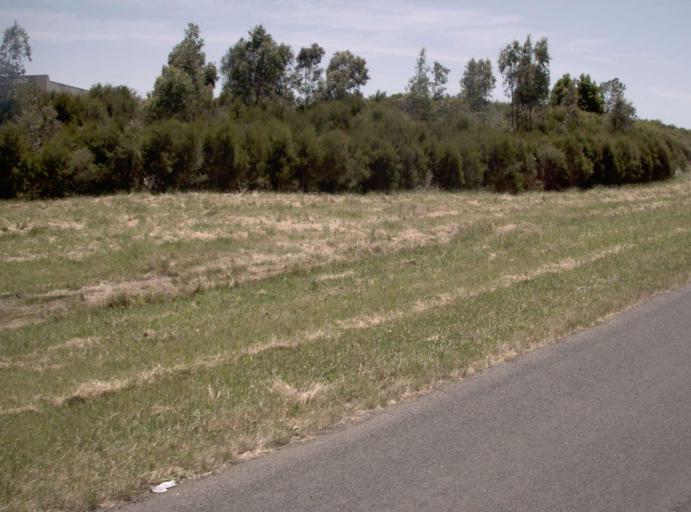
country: AU
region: Victoria
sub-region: Cardinia
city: Pakenham South
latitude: -38.0903
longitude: 145.4999
